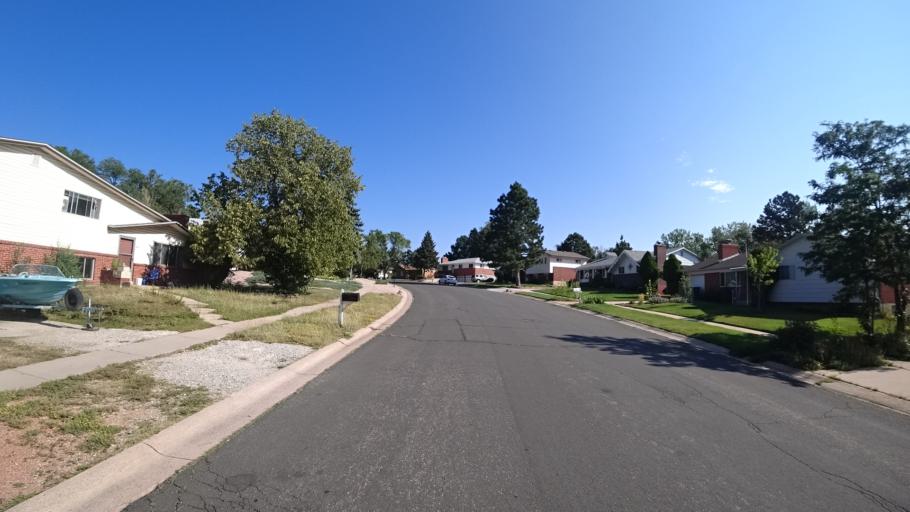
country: US
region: Colorado
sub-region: El Paso County
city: Colorado Springs
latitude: 38.8866
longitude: -104.8375
